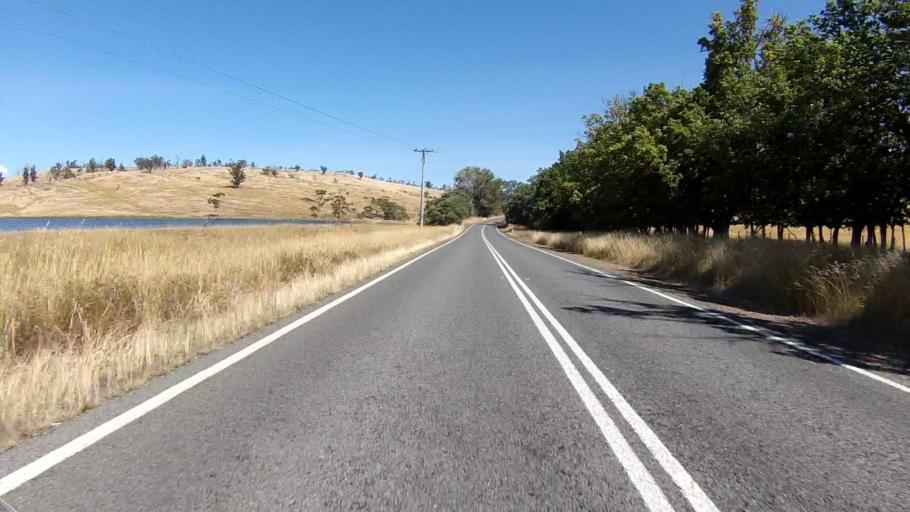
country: AU
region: Tasmania
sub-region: Sorell
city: Sorell
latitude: -42.4890
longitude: 147.9342
